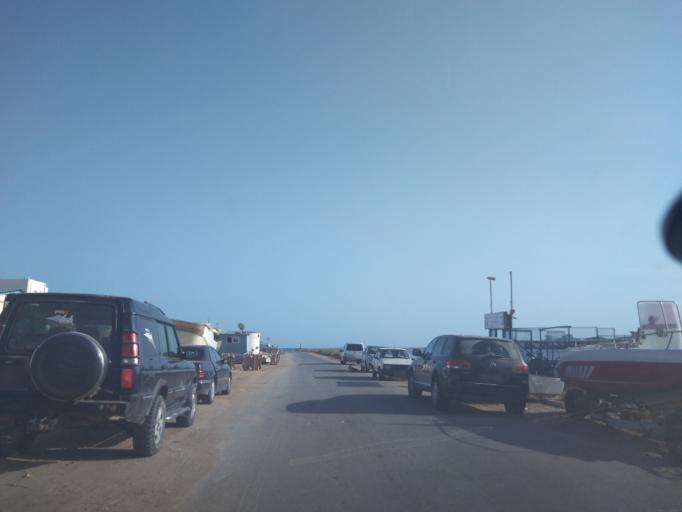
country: TN
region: Safaqis
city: Sfax
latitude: 34.7198
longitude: 10.7675
